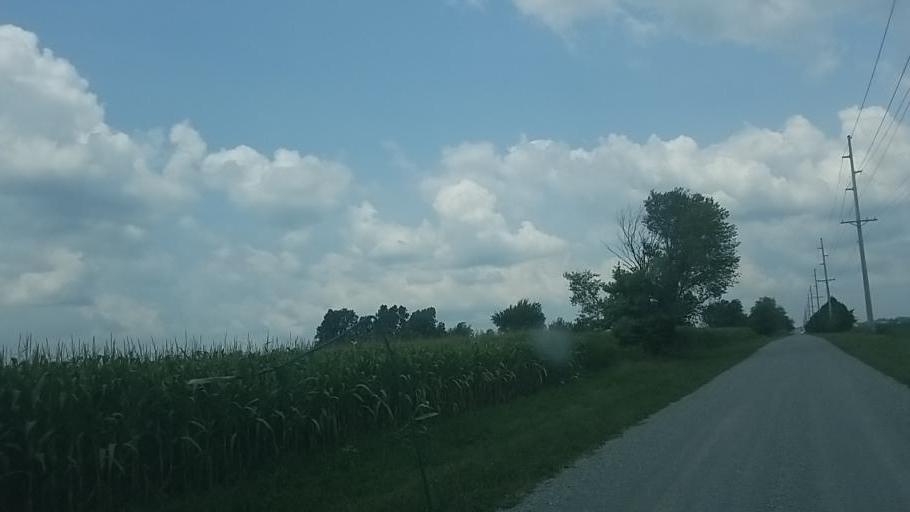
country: US
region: Ohio
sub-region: Wyandot County
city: Carey
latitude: 40.9728
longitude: -83.3048
